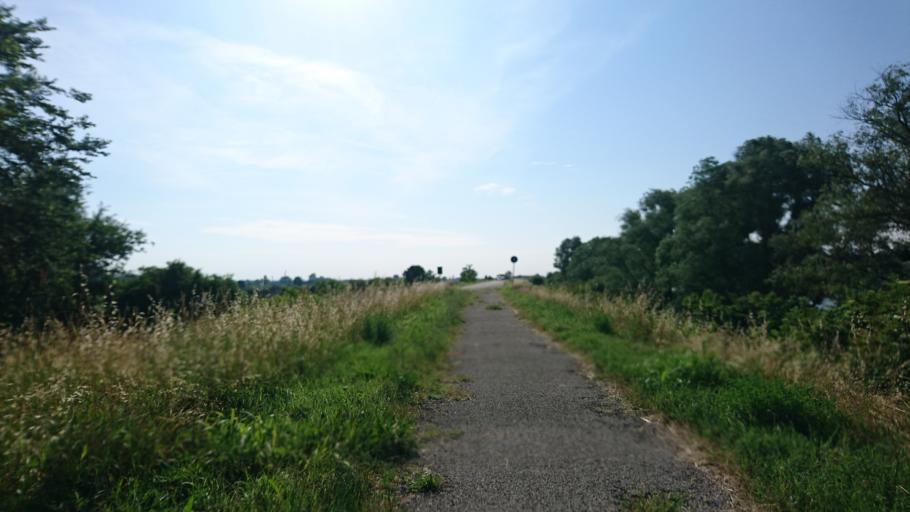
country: IT
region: Veneto
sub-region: Provincia di Verona
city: Villa Bartolomea
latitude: 45.1726
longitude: 11.3427
